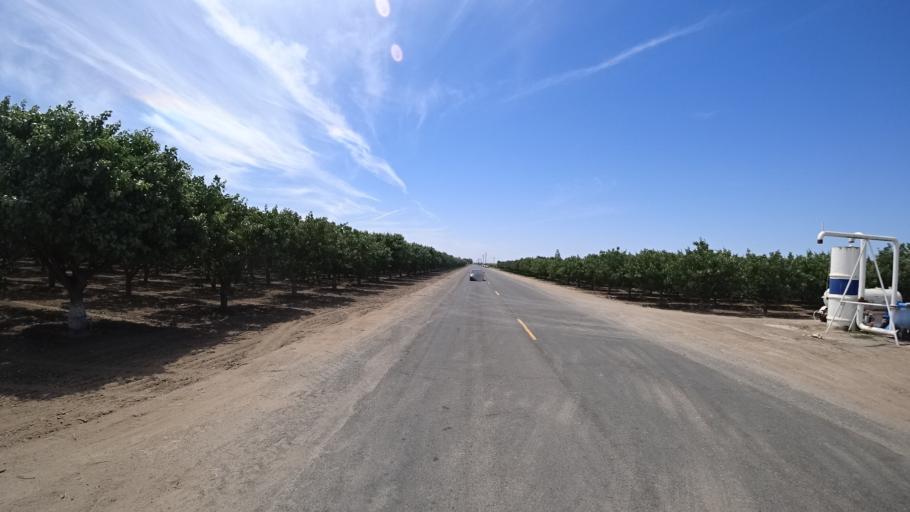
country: US
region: California
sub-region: Kings County
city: Lucerne
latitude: 36.3969
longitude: -119.6910
